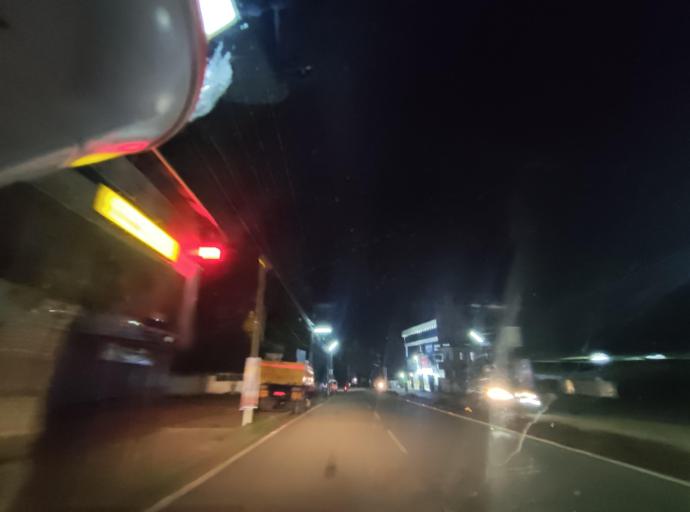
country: IN
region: Kerala
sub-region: Thiruvananthapuram
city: Nedumangad
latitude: 8.5626
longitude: 76.9435
